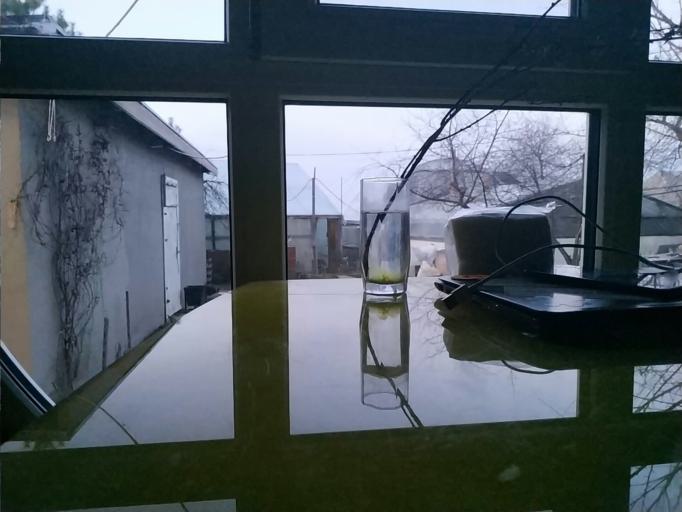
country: RU
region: Republic of Karelia
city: Sukkozero
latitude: 62.7289
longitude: 31.8765
